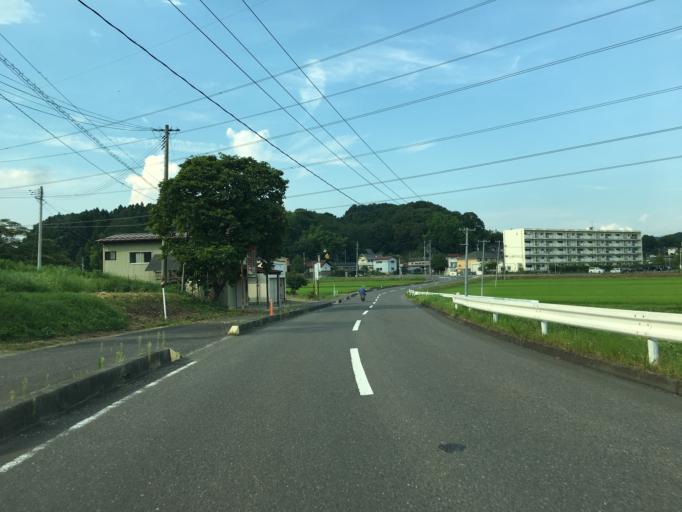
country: JP
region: Fukushima
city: Motomiya
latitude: 37.5054
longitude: 140.4333
